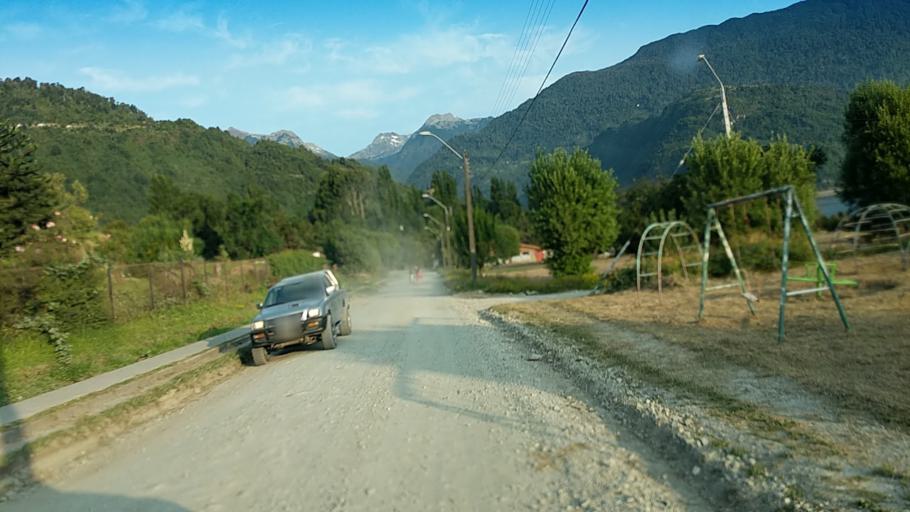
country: CL
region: Los Lagos
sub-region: Provincia de Llanquihue
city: La Ensenada
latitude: -41.4935
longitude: -72.3072
